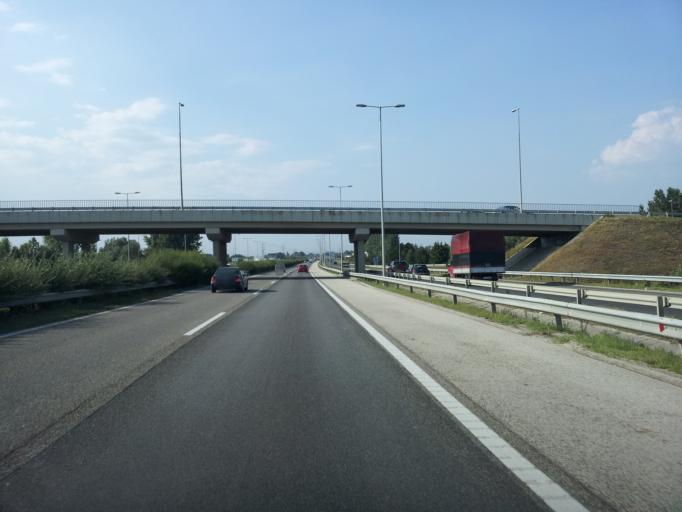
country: HU
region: Budapest
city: Budapest XVIII. keruelet
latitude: 47.4139
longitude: 19.1559
